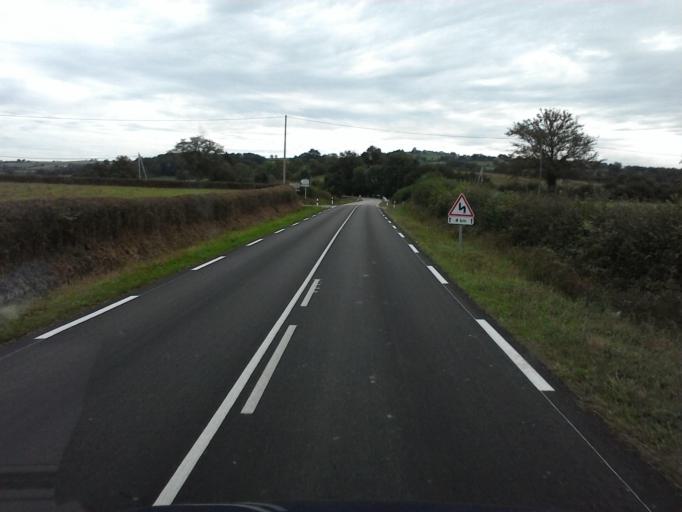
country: FR
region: Bourgogne
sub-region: Departement de Saone-et-Loire
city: Saint-Vallier
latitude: 46.6507
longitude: 4.4238
